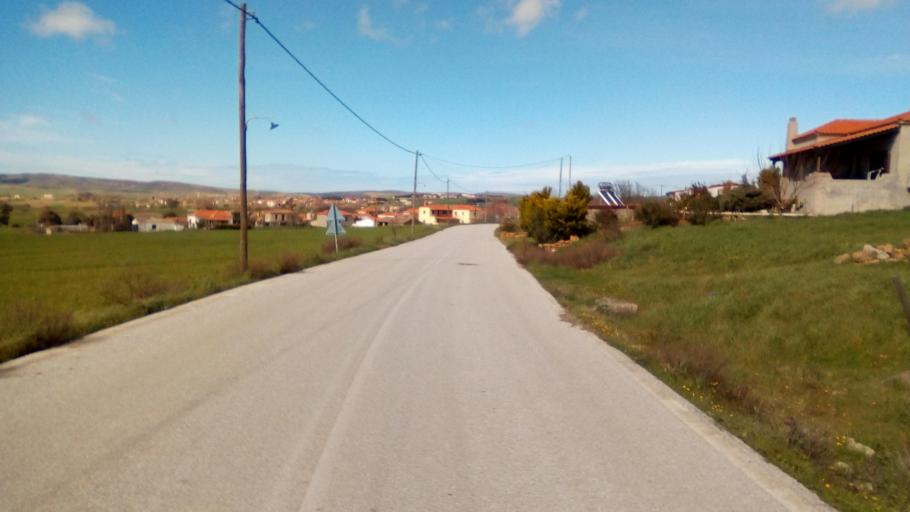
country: GR
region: North Aegean
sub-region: Nomos Lesvou
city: Myrina
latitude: 39.9311
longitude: 25.2310
